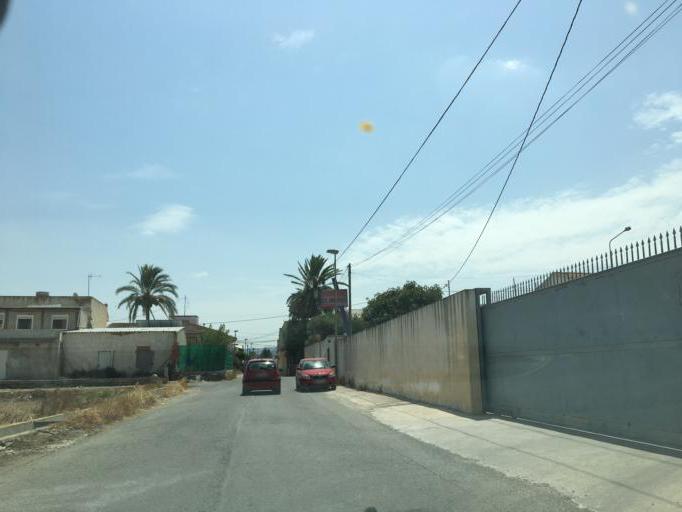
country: ES
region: Murcia
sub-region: Murcia
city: Santomera
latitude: 38.0287
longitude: -1.0496
